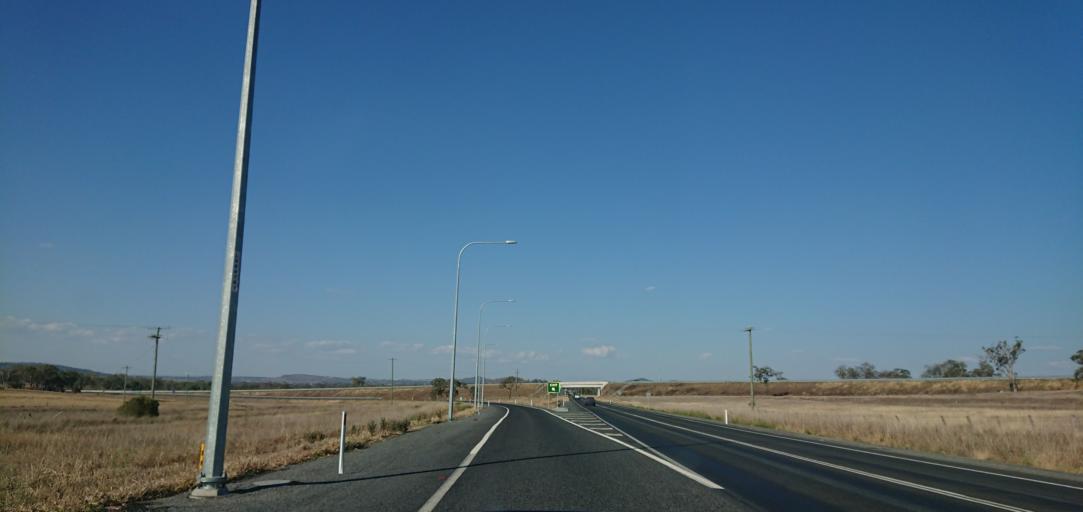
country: AU
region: Queensland
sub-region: Toowoomba
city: Westbrook
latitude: -27.6162
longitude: 151.7813
